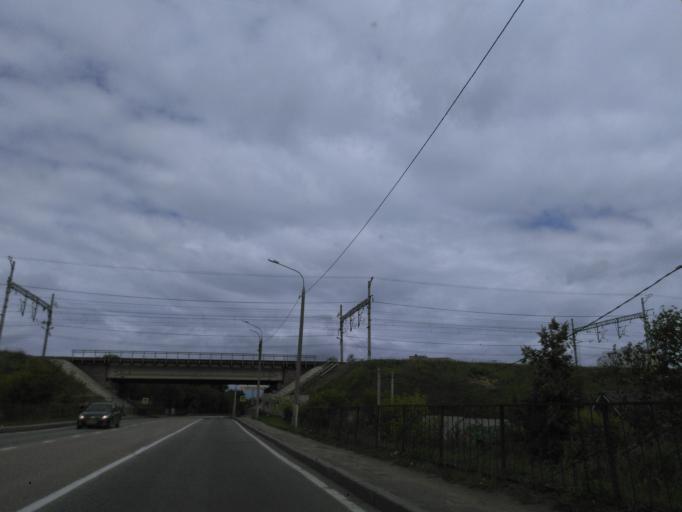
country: RU
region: Moskovskaya
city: Solnechnogorsk
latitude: 56.1877
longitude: 36.9639
